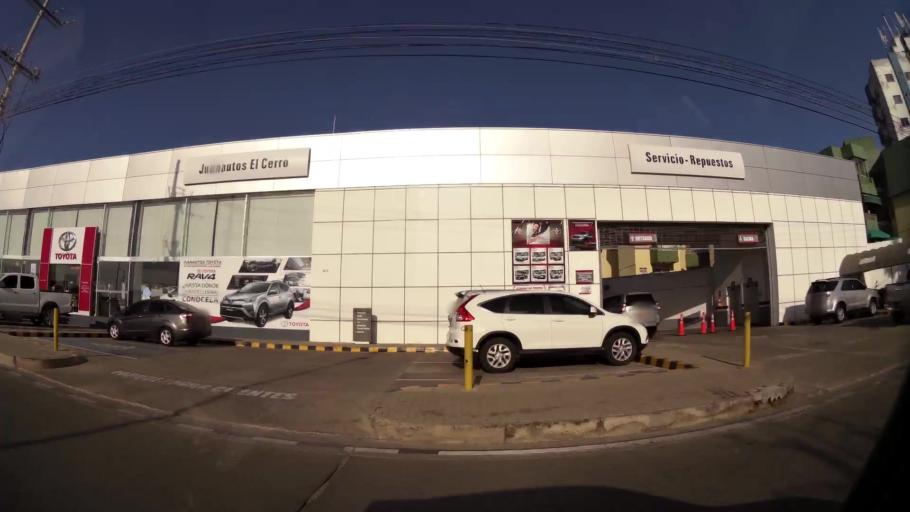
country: CO
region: Bolivar
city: Cartagena
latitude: 10.4195
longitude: -75.5360
